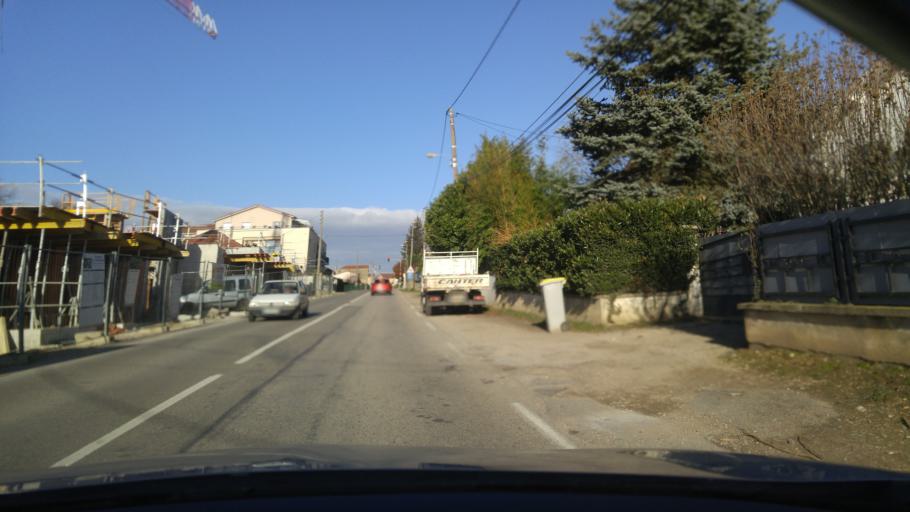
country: FR
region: Rhone-Alpes
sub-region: Departement de l'Isere
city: Tignieu-Jameyzieu
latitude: 45.7322
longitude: 5.1868
